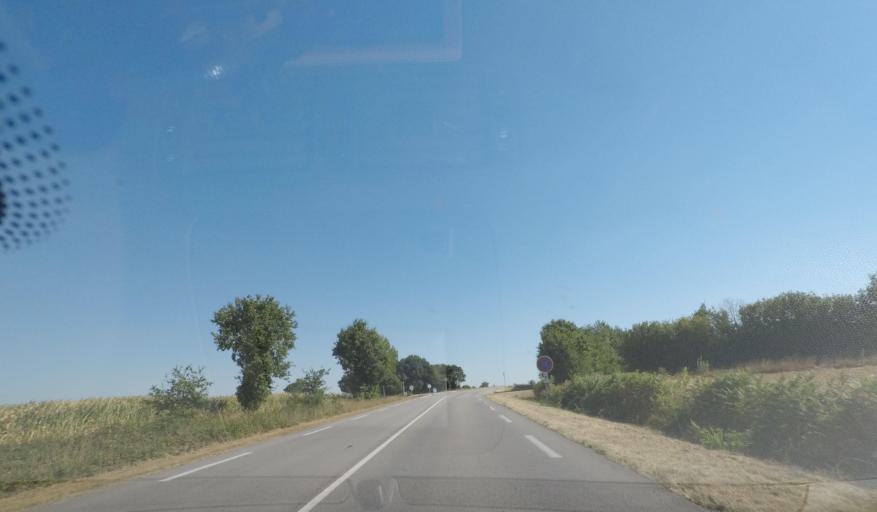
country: FR
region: Brittany
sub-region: Departement du Morbihan
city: Peaule
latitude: 47.5919
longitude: -2.3766
